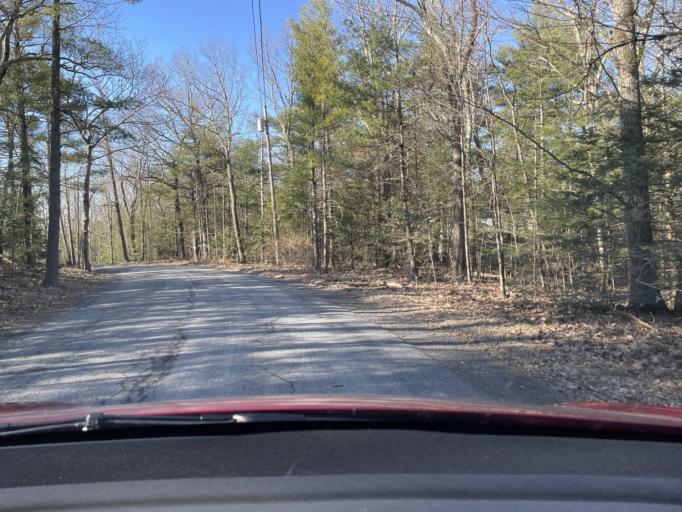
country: US
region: New York
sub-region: Ulster County
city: Zena
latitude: 42.0670
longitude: -74.0701
